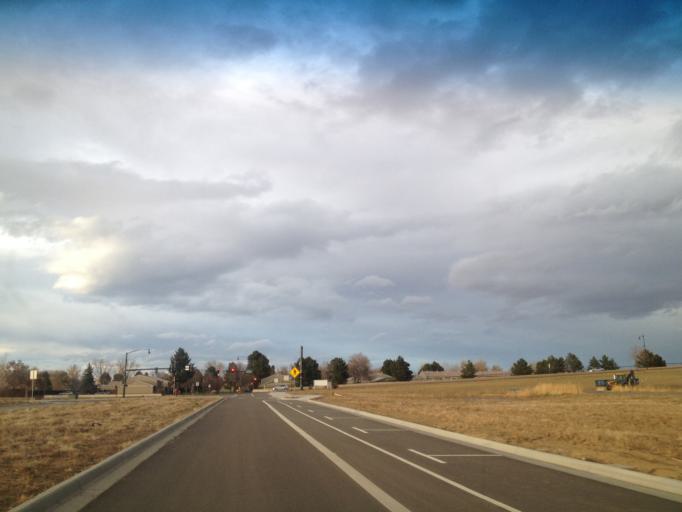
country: US
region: Colorado
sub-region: Adams County
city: Westminster
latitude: 39.8620
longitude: -105.0596
